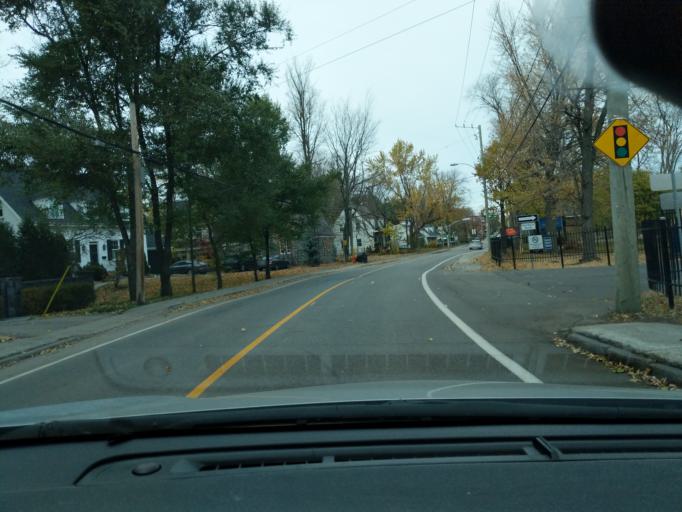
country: CA
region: Quebec
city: Quebec
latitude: 46.7776
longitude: -71.2520
